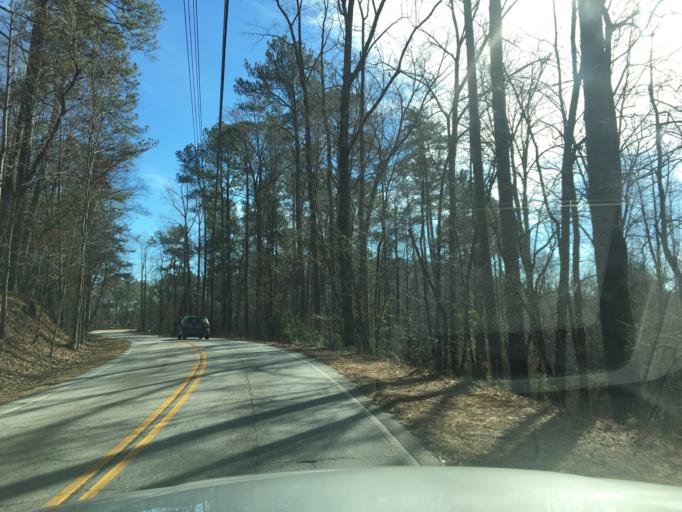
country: US
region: Georgia
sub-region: Rockdale County
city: Lakeview Estates
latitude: 33.7623
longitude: -84.0508
